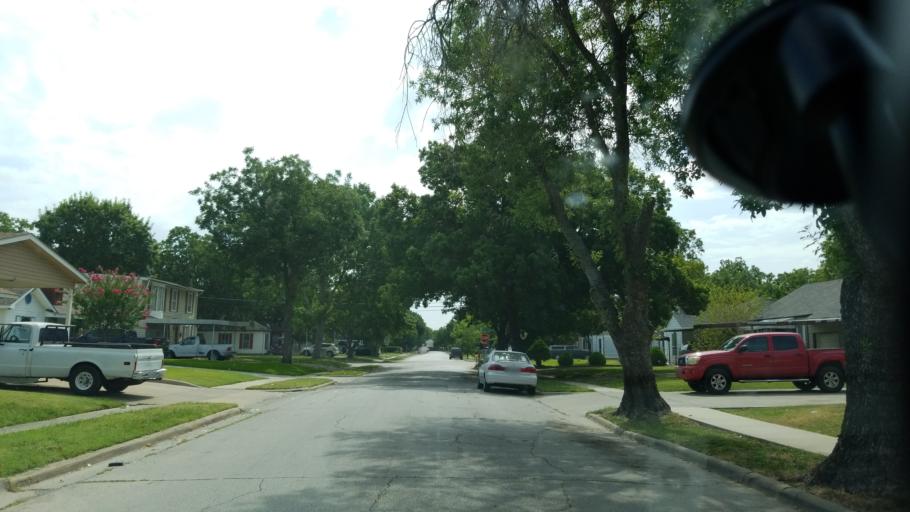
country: US
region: Texas
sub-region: Dallas County
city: Grand Prairie
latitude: 32.7507
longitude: -96.9894
